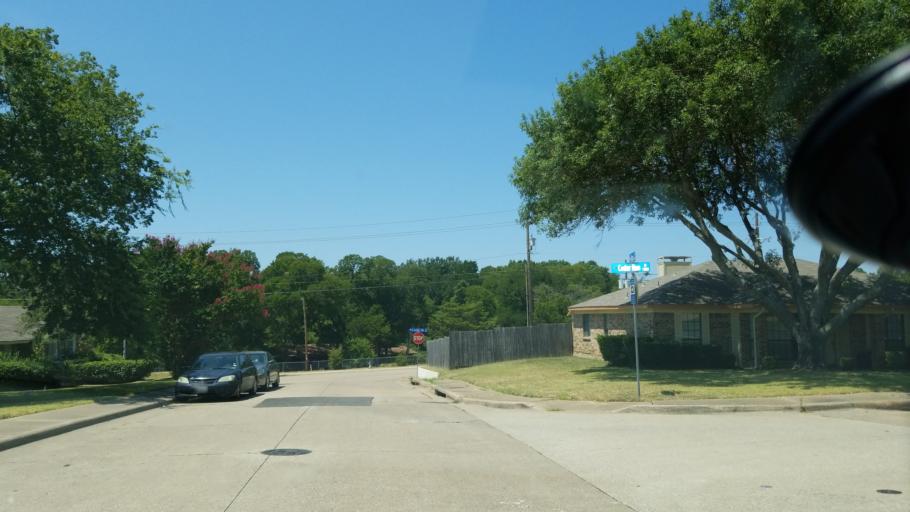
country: US
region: Texas
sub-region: Dallas County
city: Duncanville
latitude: 32.6352
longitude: -96.8906
